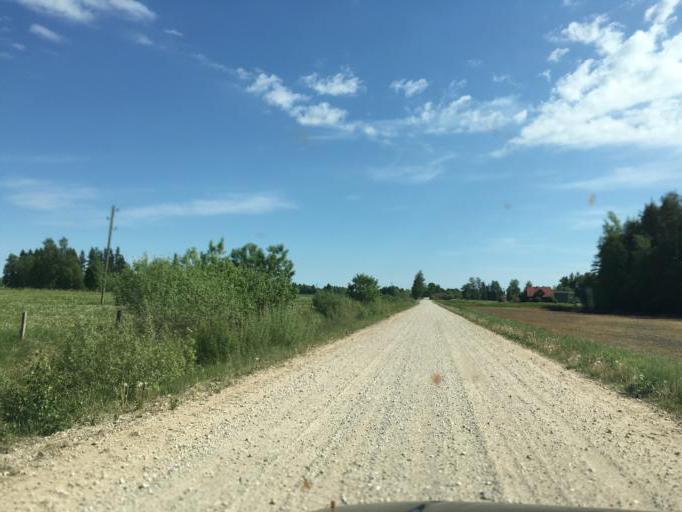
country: LV
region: Talsu Rajons
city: Valdemarpils
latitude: 57.3364
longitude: 22.4788
